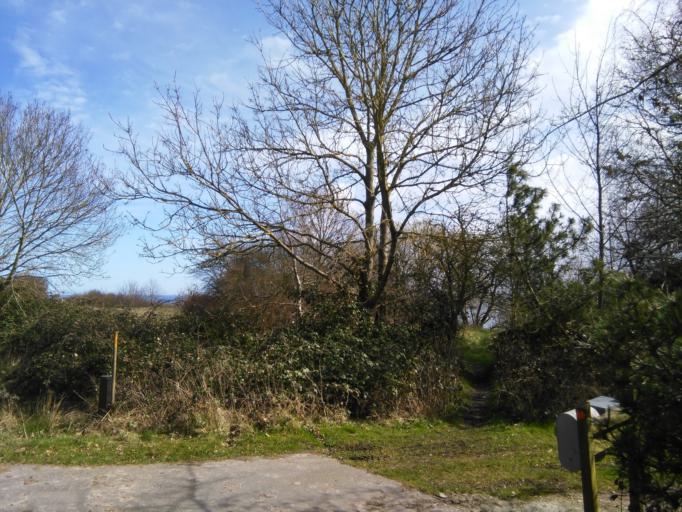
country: DK
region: Central Jutland
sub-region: Arhus Kommune
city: Malling
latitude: 55.9989
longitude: 10.2569
